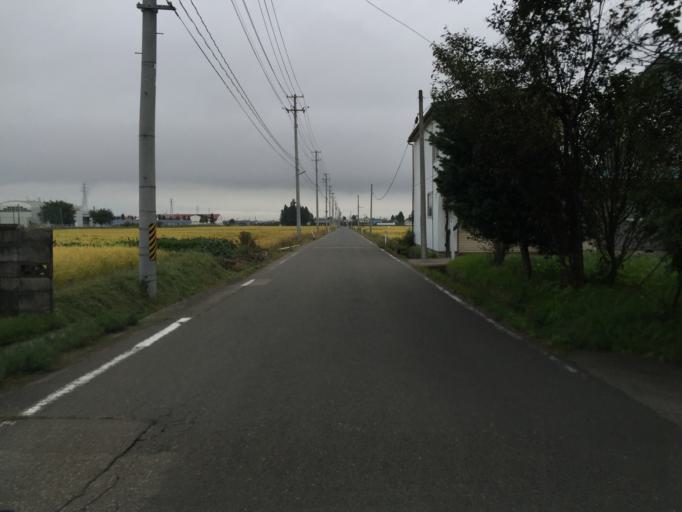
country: JP
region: Fukushima
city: Kitakata
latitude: 37.4623
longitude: 139.9150
